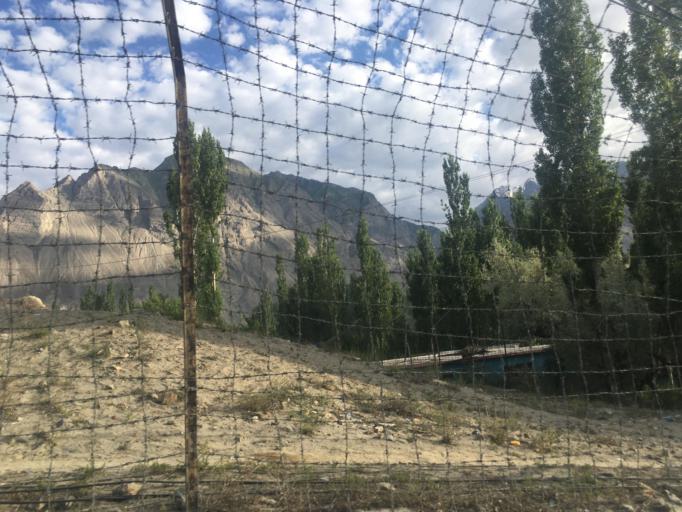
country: PK
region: Gilgit-Baltistan
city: Skardu
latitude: 35.2952
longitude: 75.6129
